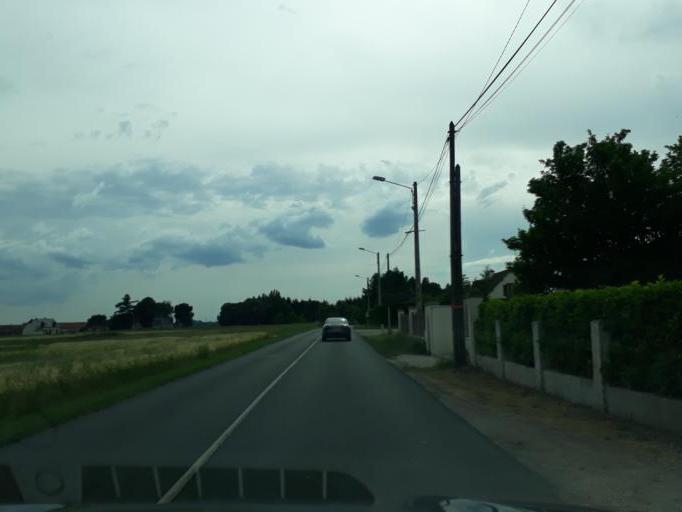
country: FR
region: Centre
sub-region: Departement du Loiret
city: Sandillon
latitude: 47.8430
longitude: 2.0186
